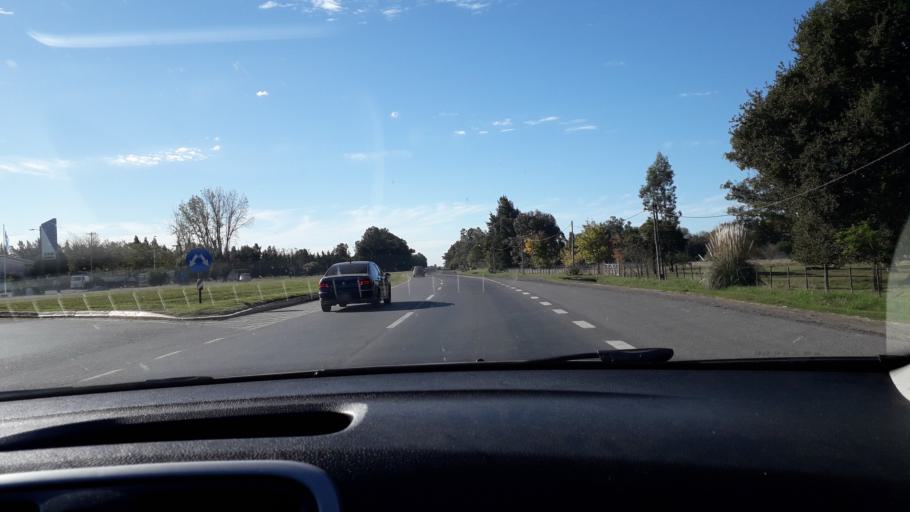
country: AR
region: Buenos Aires
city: Canuelas
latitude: -35.1091
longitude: -58.7347
